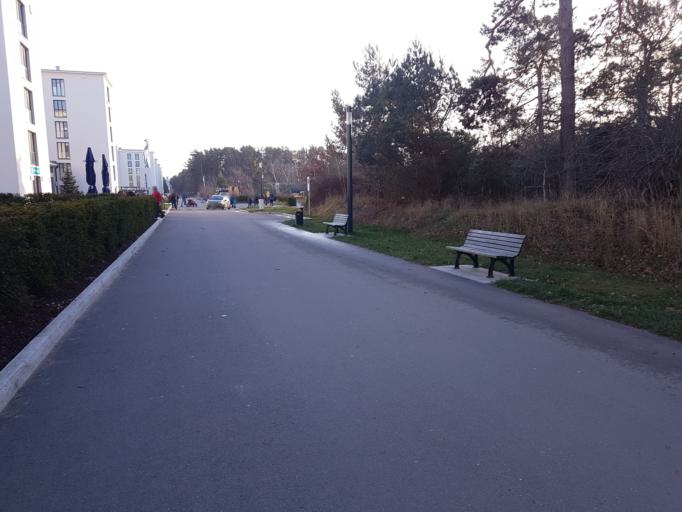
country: DE
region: Mecklenburg-Vorpommern
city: Ostseebad Binz
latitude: 54.4317
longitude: 13.5797
